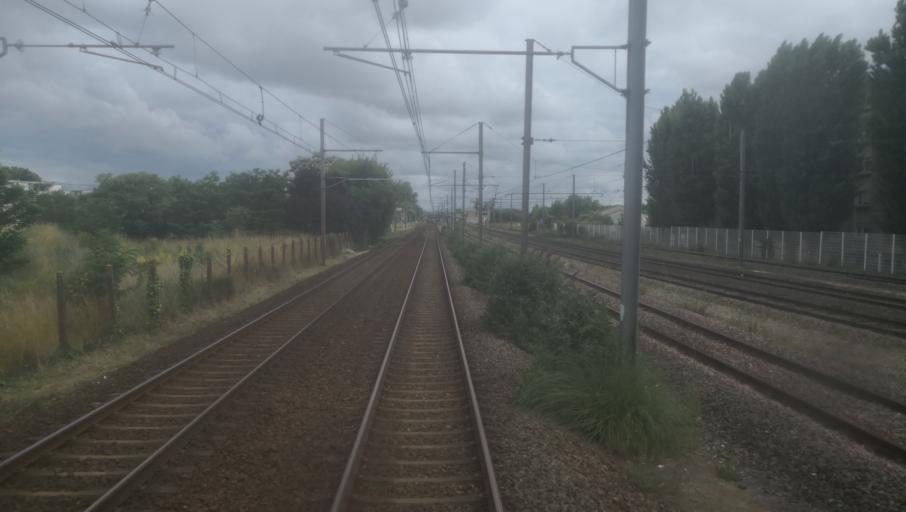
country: FR
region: Aquitaine
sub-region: Departement de la Gironde
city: Begles
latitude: 44.7978
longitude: -0.5547
